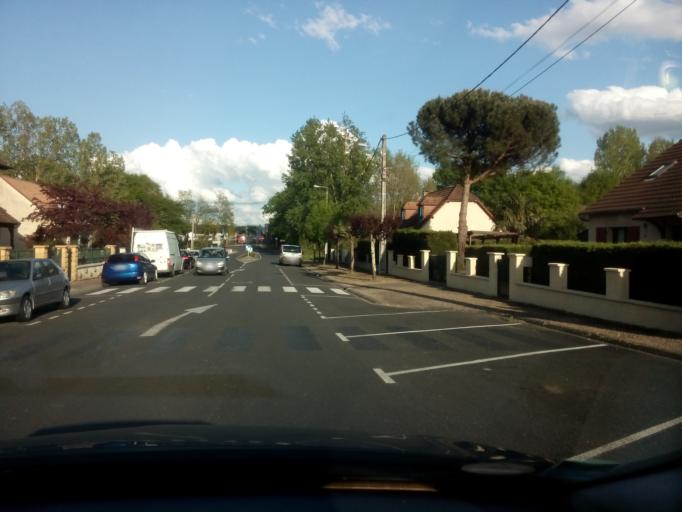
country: FR
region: Limousin
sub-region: Departement de la Correze
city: Saint-Pantaleon-de-Larche
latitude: 45.1438
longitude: 1.4657
